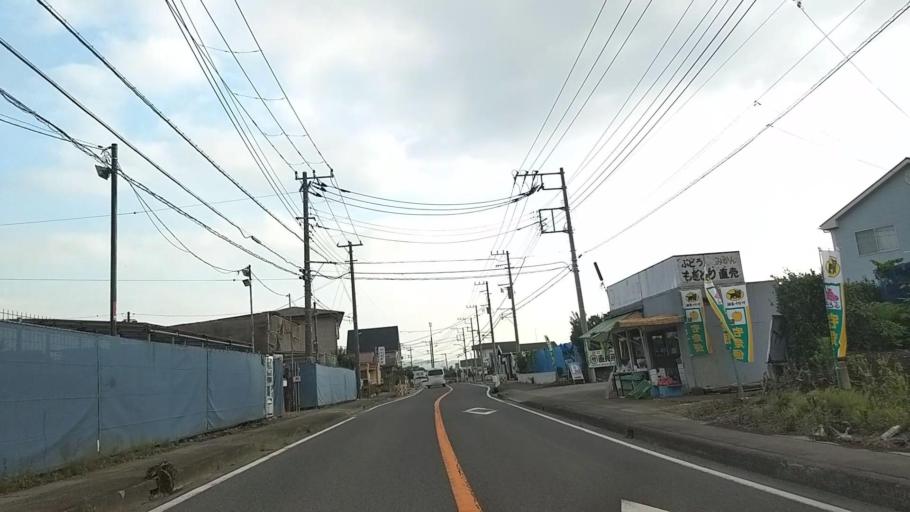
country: JP
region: Kanagawa
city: Isehara
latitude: 35.3826
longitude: 139.3012
